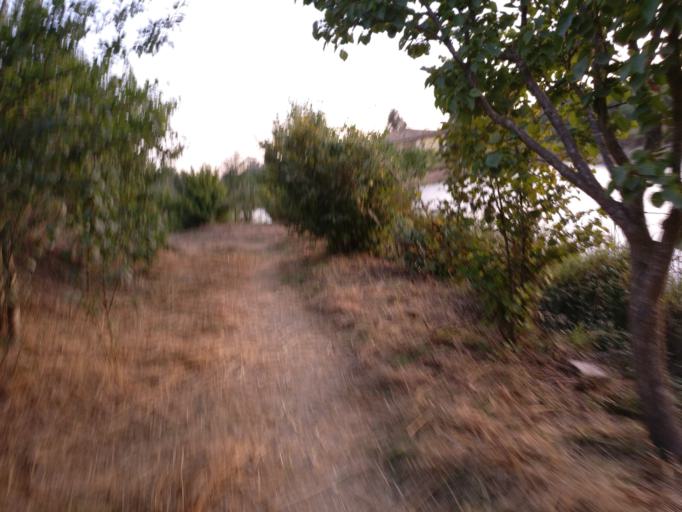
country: PT
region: Beja
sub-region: Odemira
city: Odemira
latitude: 37.7189
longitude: -8.5176
